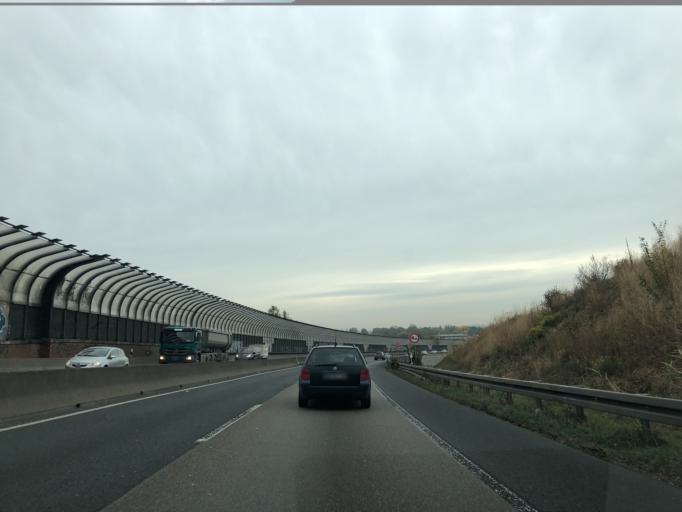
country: DE
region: Hesse
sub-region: Regierungsbezirk Darmstadt
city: Frankfurt am Main
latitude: 50.1373
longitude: 8.7182
